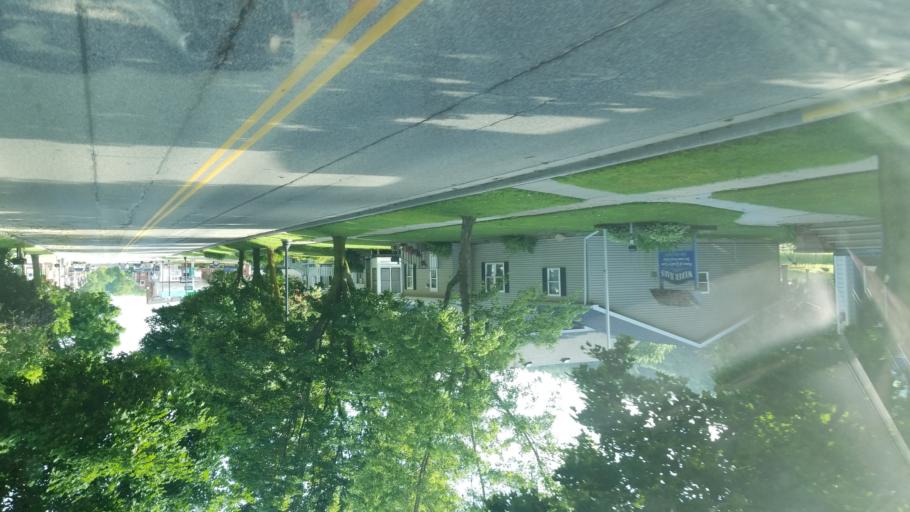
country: US
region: Wisconsin
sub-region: Juneau County
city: Elroy
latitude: 43.6555
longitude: -90.2234
